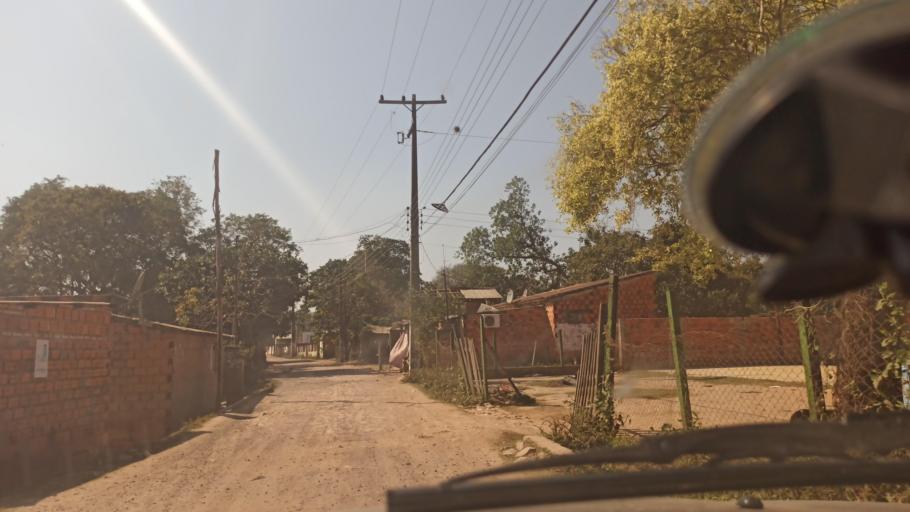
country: AR
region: Formosa
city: Clorinda
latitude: -25.2936
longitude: -57.6976
